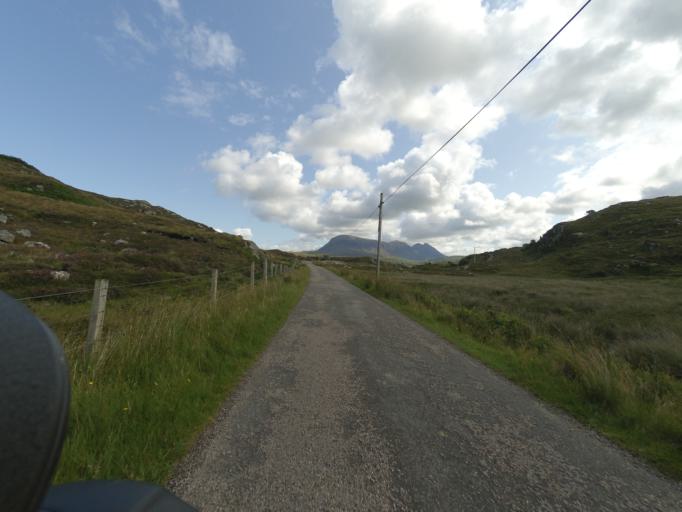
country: GB
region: Scotland
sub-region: Highland
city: Ullapool
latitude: 58.2418
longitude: -5.1837
